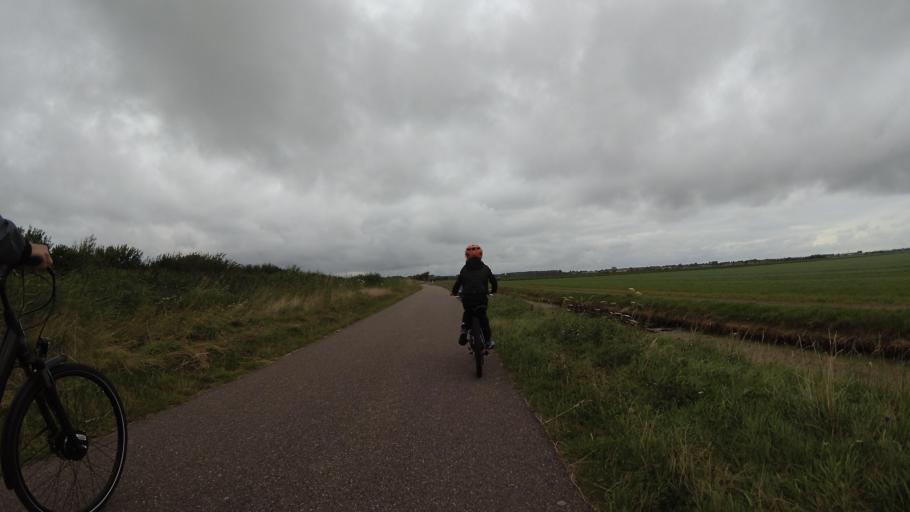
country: NL
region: North Holland
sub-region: Gemeente Den Helder
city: Den Helder
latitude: 52.9175
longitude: 4.7288
